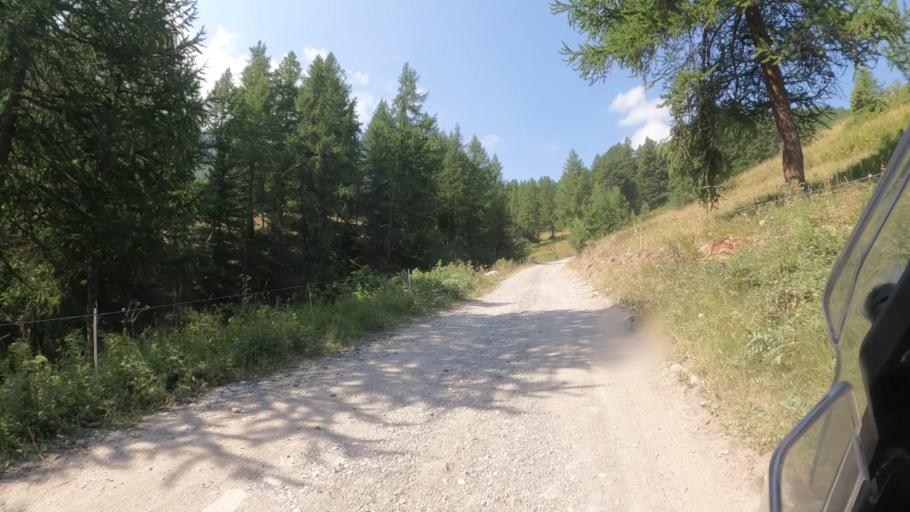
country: IT
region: Piedmont
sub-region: Provincia di Torino
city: Cesana Torinese
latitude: 44.9215
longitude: 6.8086
